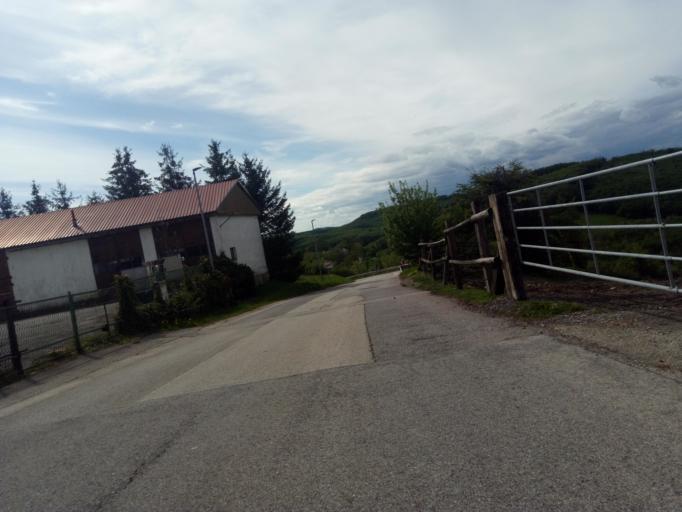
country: AT
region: Lower Austria
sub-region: Politischer Bezirk Wien-Umgebung
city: Wolfsgraben
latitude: 48.1307
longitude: 16.1118
